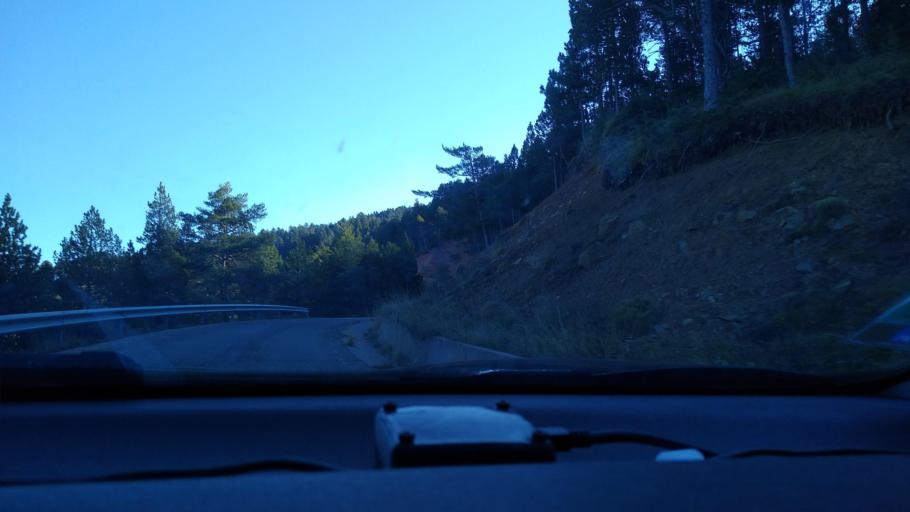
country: ES
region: Catalonia
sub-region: Provincia de Barcelona
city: Saldes
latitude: 42.2055
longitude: 1.7333
